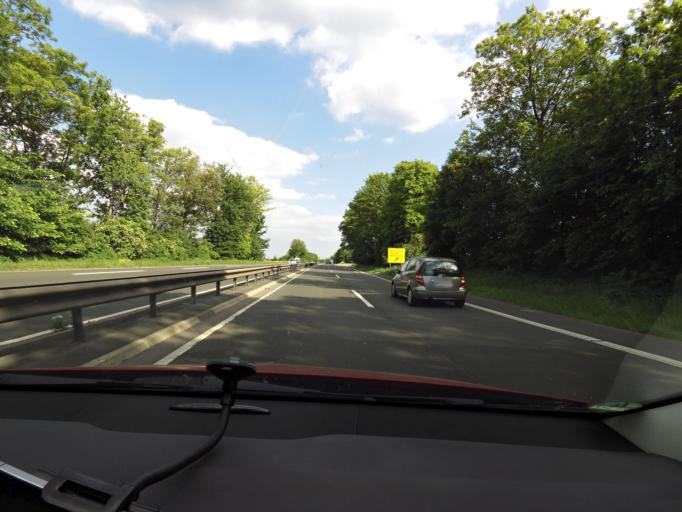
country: DE
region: Rheinland-Pfalz
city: Weissenthurm
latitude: 50.4143
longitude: 7.4355
